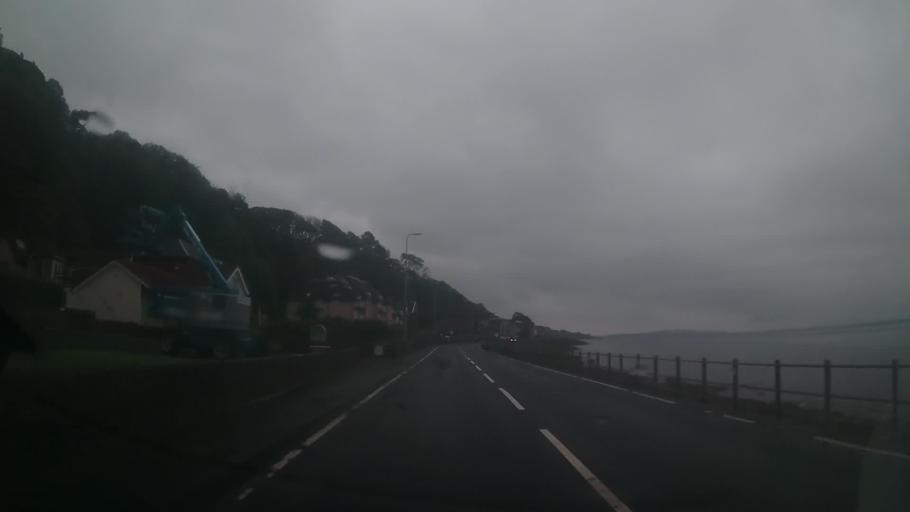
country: GB
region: Scotland
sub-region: North Ayrshire
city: Skelmorlie
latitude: 55.8623
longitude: -4.8901
